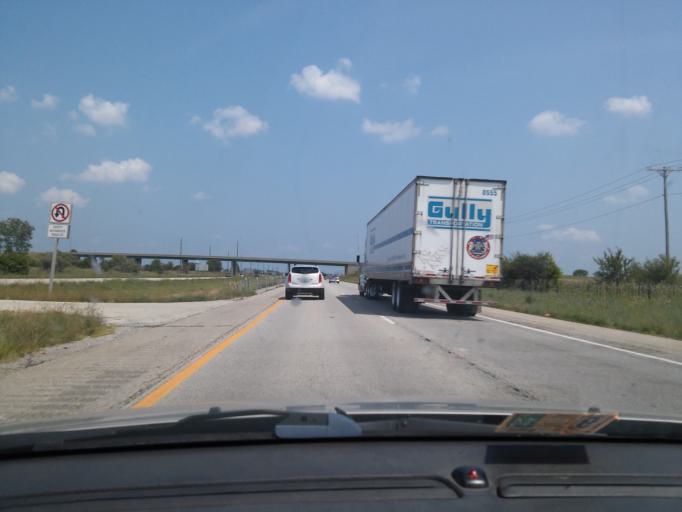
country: US
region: Illinois
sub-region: Sangamon County
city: Jerome
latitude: 39.7418
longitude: -89.6909
